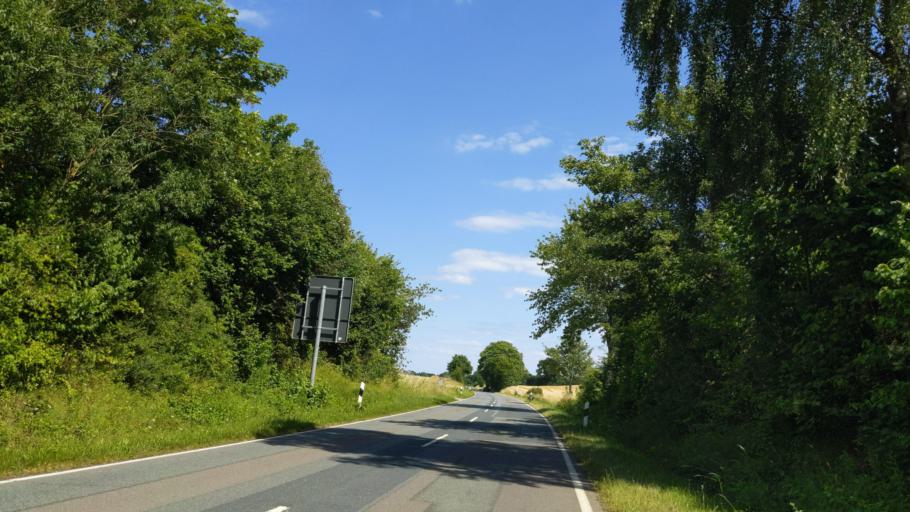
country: DE
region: Schleswig-Holstein
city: Gromitz
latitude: 54.1564
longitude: 10.9251
